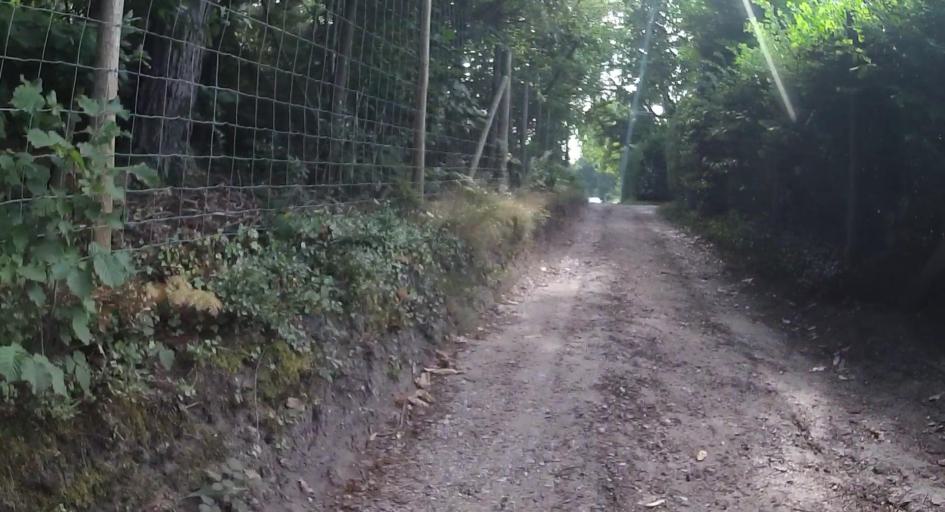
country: GB
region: England
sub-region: Surrey
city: Farnham
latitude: 51.1940
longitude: -0.8049
